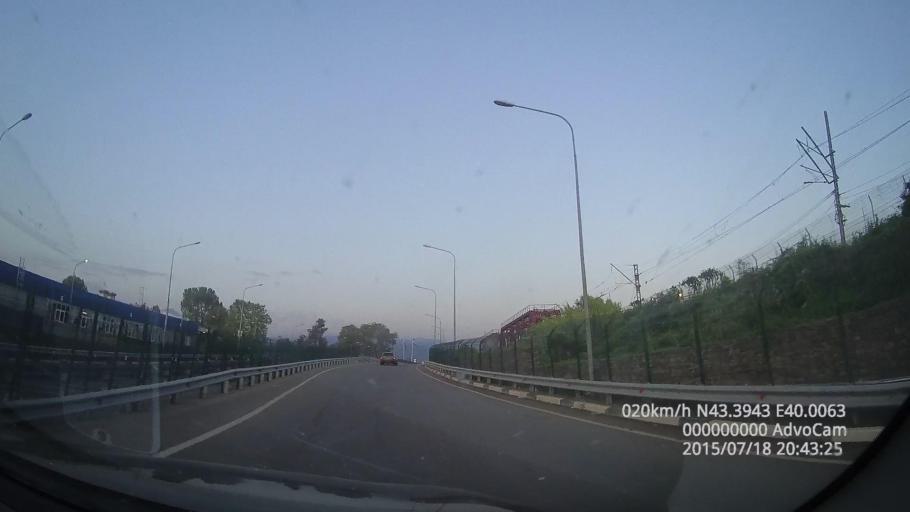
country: GE
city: Gantiadi
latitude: 43.3941
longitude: 40.0074
